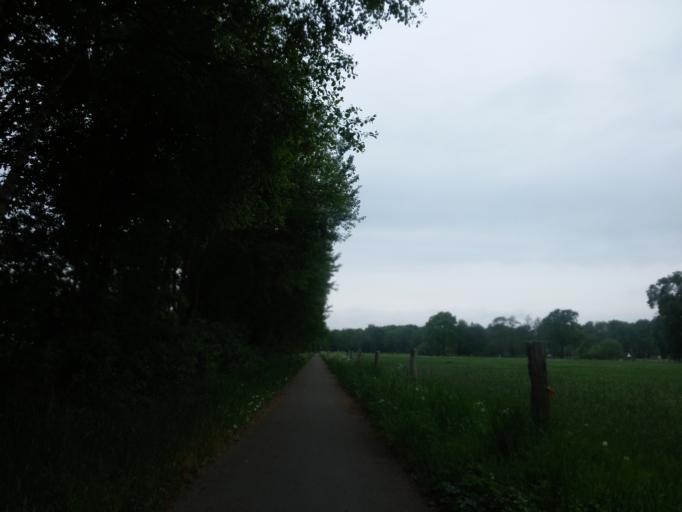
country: DE
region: Lower Saxony
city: Wietmarschen
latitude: 52.5082
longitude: 7.1246
